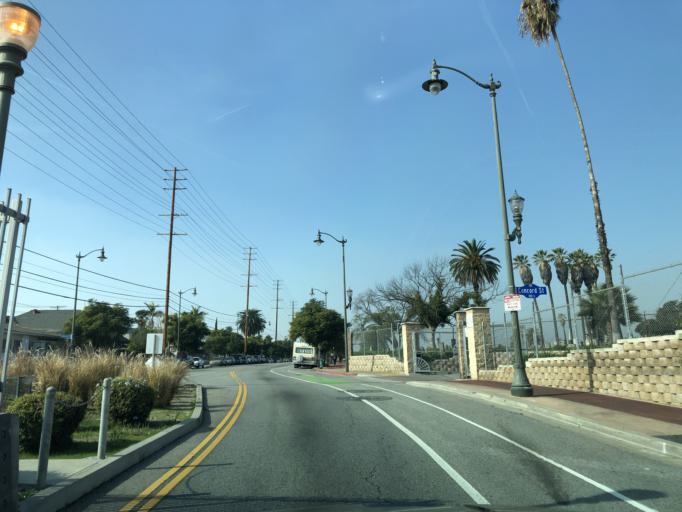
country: US
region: California
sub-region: Los Angeles County
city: Boyle Heights
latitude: 34.0377
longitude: -118.1960
